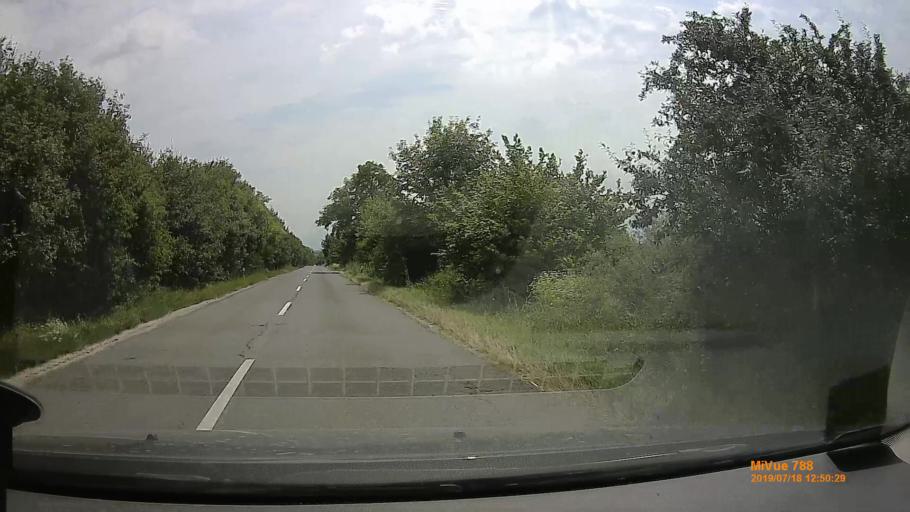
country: HU
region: Pest
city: Perbal
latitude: 47.5679
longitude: 18.7905
